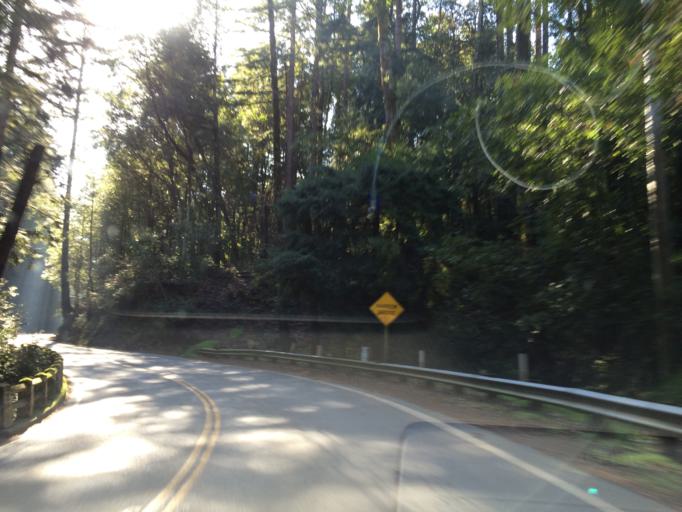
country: US
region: California
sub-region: Santa Cruz County
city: Boulder Creek
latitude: 37.1439
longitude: -122.1561
